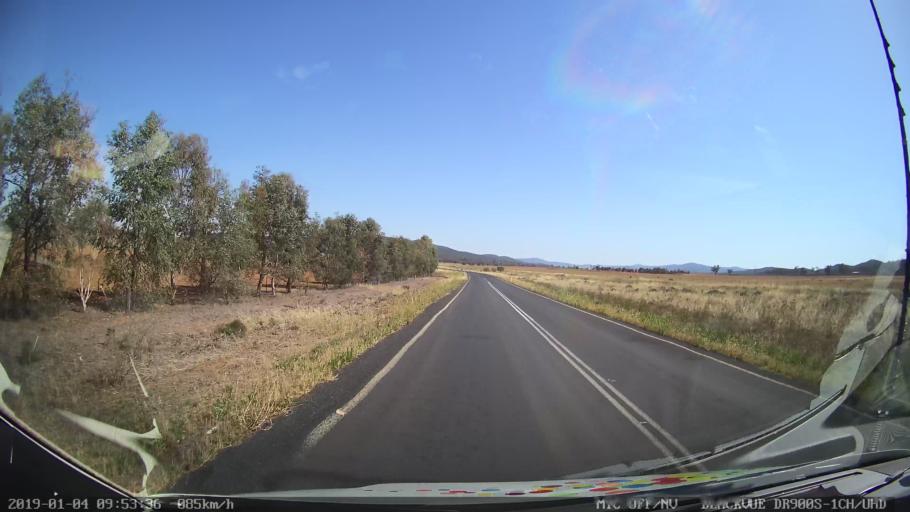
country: AU
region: New South Wales
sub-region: Cabonne
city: Canowindra
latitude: -33.5507
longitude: 148.4197
